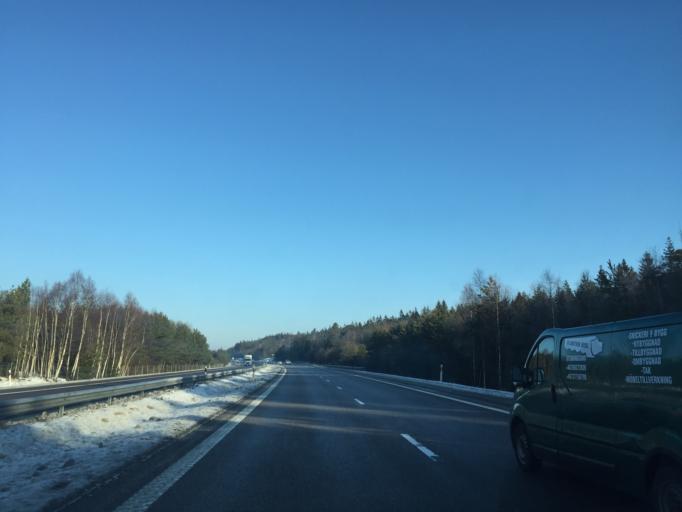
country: SE
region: Vaestra Goetaland
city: Svanesund
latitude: 58.1309
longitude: 11.8857
